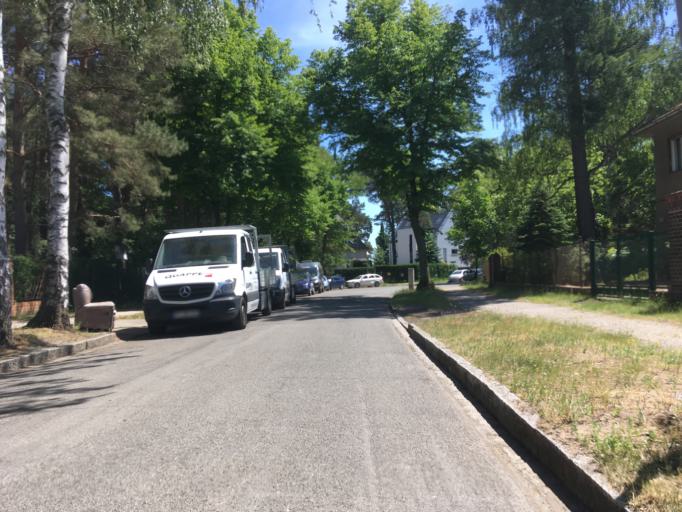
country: DE
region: Berlin
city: Schmockwitz
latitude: 52.3905
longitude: 13.6405
